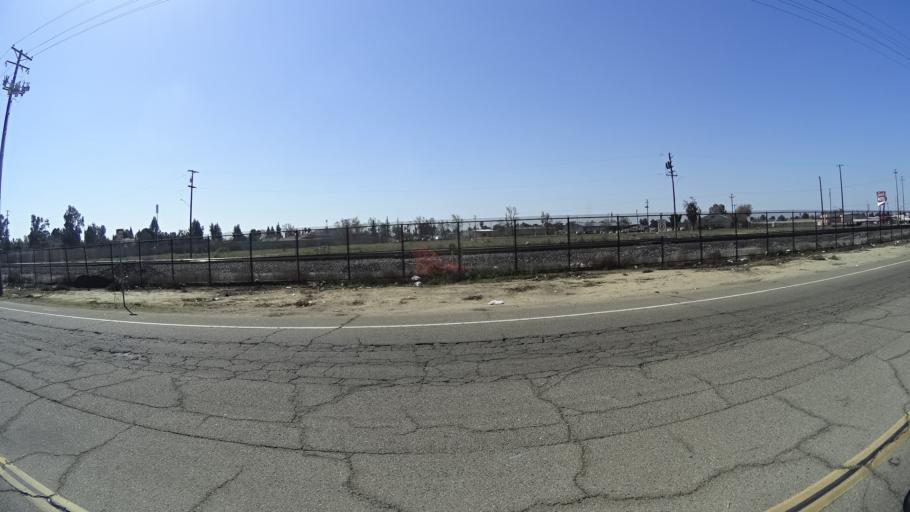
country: US
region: California
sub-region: Fresno County
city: Fresno
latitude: 36.7614
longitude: -119.8248
